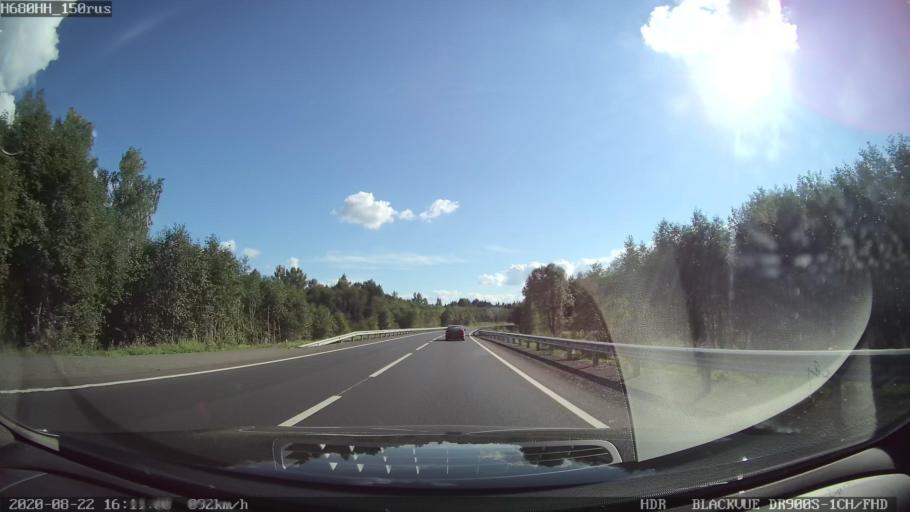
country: RU
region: Tverskaya
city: Rameshki
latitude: 57.5065
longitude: 36.2677
